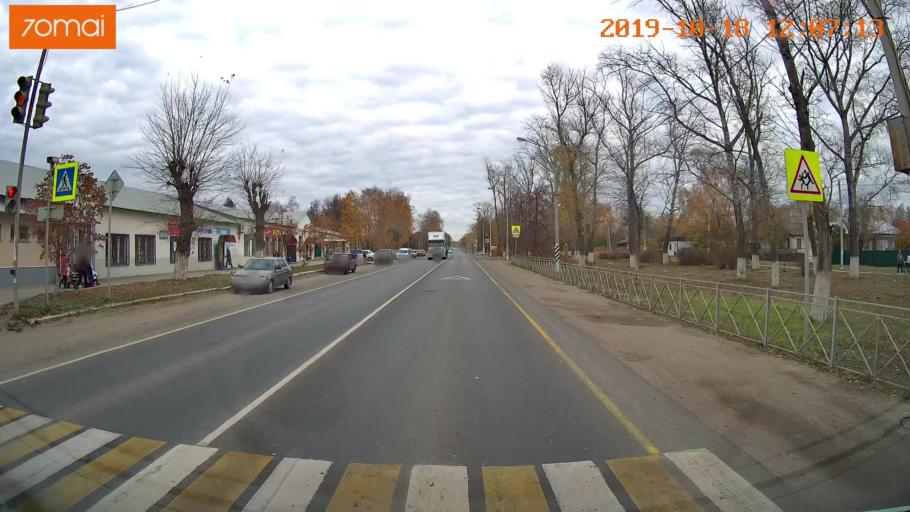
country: RU
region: Rjazan
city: Zakharovo
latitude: 54.3684
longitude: 39.2775
